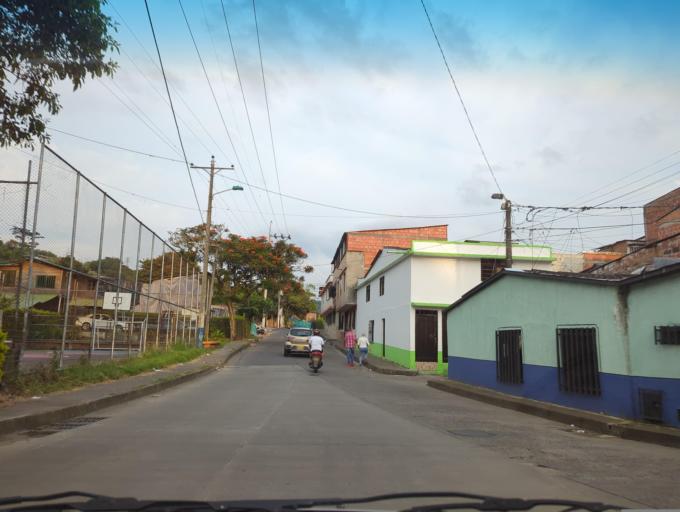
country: CO
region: Risaralda
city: Pereira
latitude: 4.8194
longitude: -75.7154
